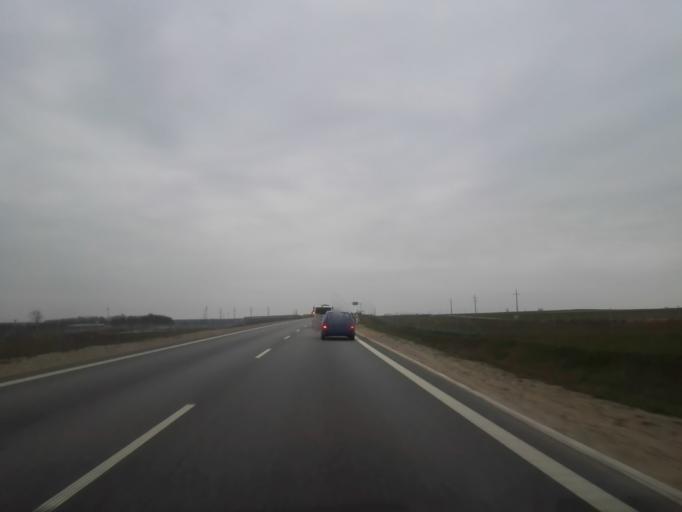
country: PL
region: Podlasie
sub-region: Powiat kolnenski
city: Stawiski
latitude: 53.3972
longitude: 22.1546
